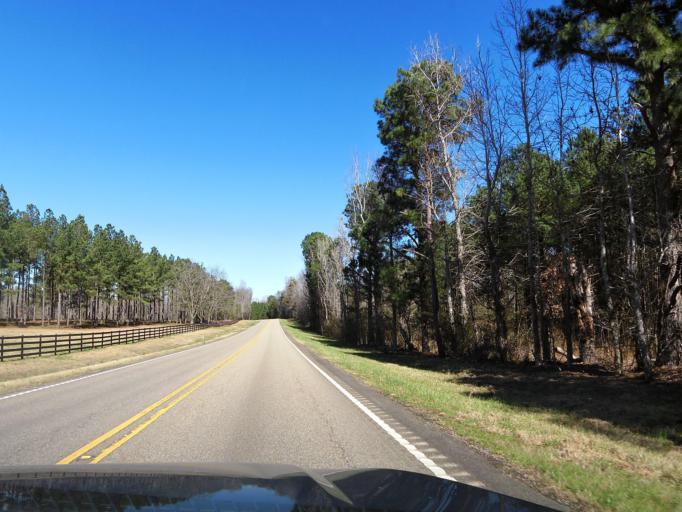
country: US
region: Alabama
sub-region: Bullock County
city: Union Springs
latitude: 32.1305
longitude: -85.7688
